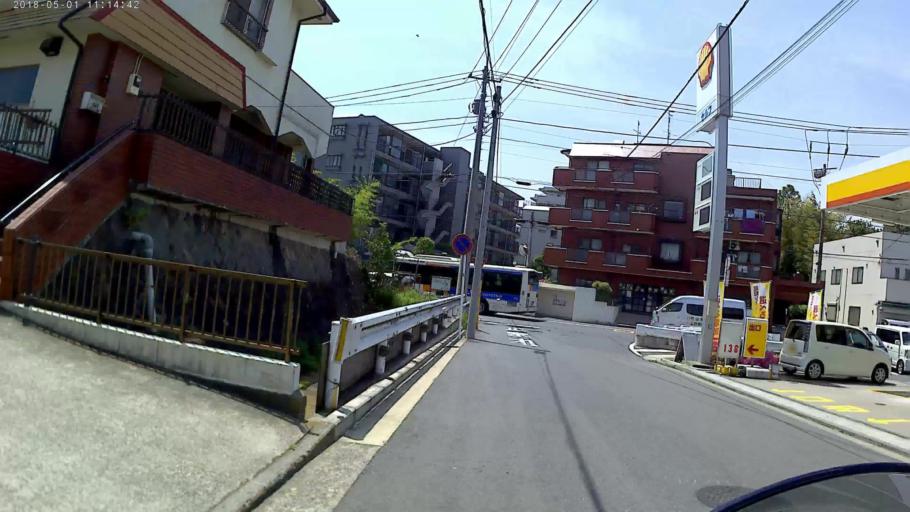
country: JP
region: Kanagawa
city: Minami-rinkan
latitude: 35.4888
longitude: 139.5423
